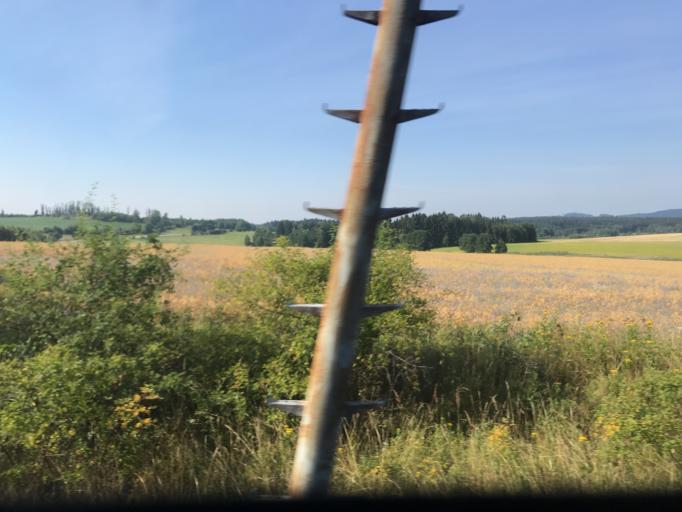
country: CZ
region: Jihocesky
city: Chotoviny
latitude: 49.5352
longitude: 14.6577
